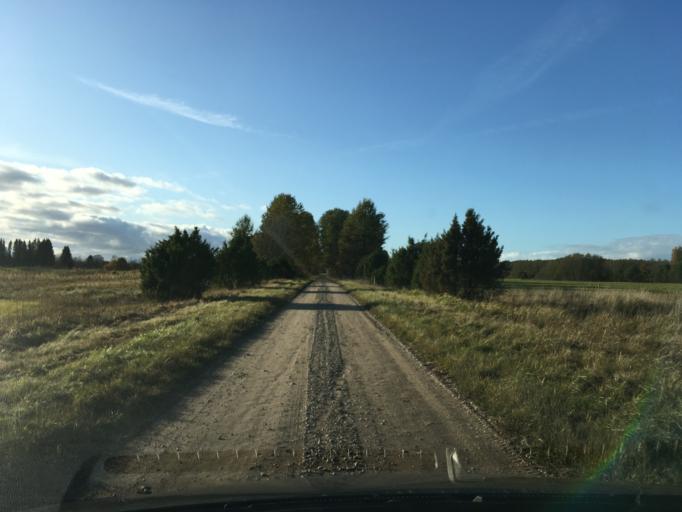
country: EE
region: Laeaene
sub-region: Lihula vald
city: Lihula
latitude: 58.5639
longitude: 23.7983
